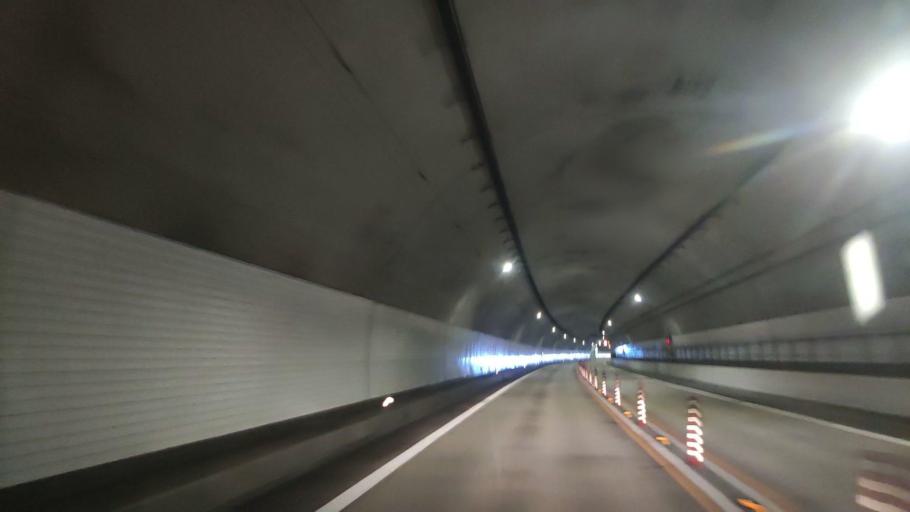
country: JP
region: Kyoto
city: Miyazu
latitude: 35.5544
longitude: 135.1296
